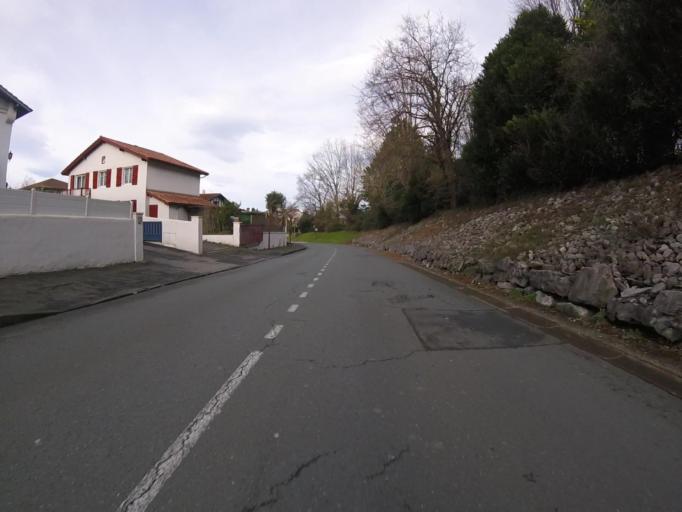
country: FR
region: Aquitaine
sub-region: Departement des Pyrenees-Atlantiques
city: Saint-Jean-de-Luz
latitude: 43.3781
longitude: -1.6591
